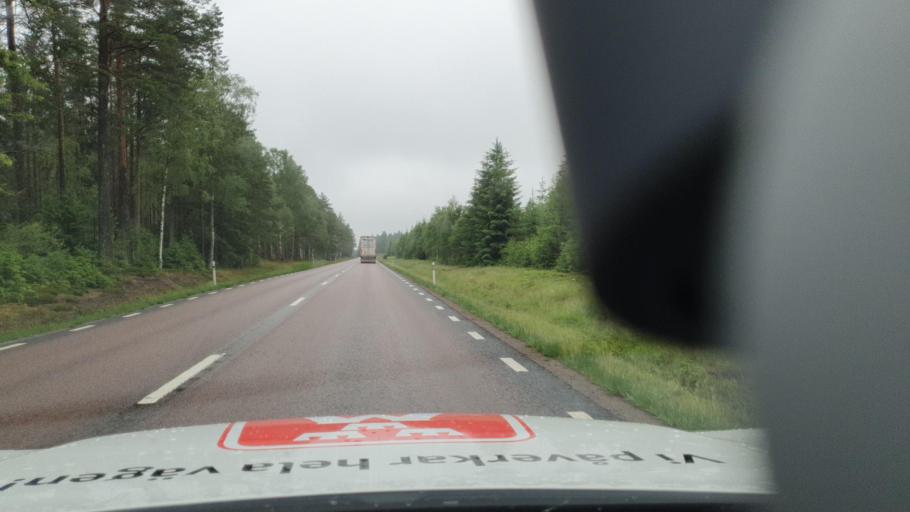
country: SE
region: Vaermland
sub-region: Kristinehamns Kommun
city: Bjorneborg
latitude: 59.2448
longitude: 14.1780
